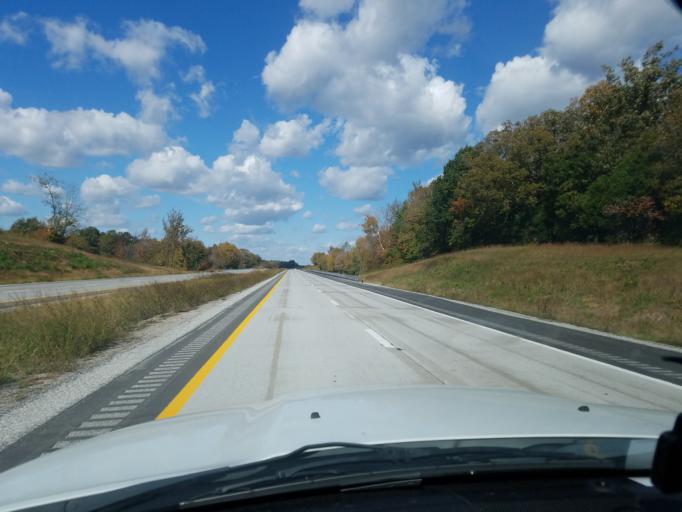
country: US
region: Kentucky
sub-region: Ohio County
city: Oak Grove
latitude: 37.3601
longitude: -86.7928
